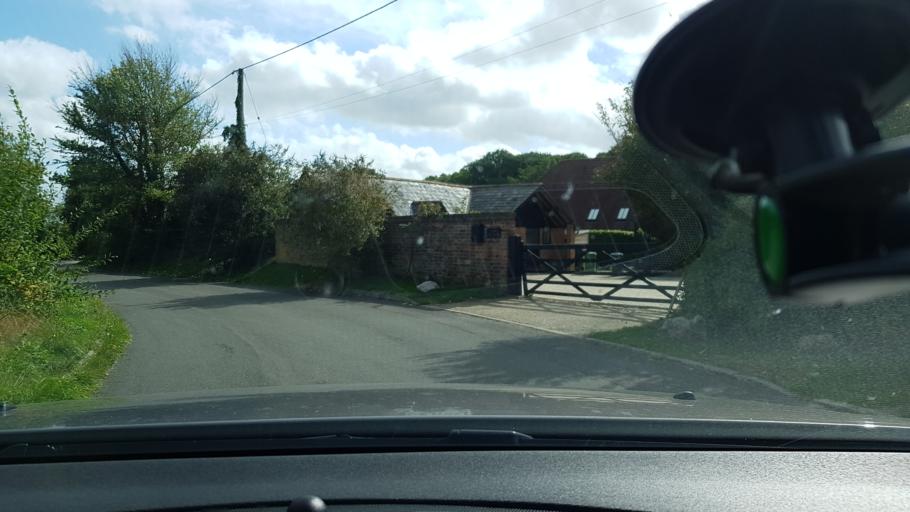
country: GB
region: England
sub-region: Wiltshire
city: Chilton Foliat
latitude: 51.4583
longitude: -1.5023
